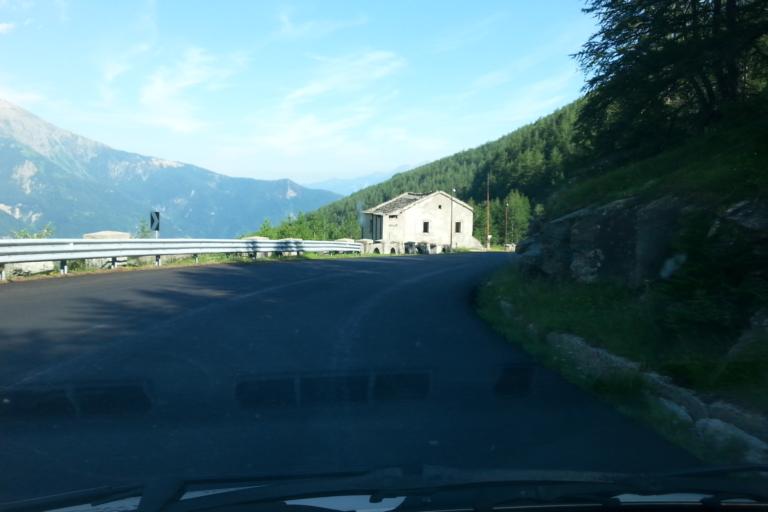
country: IT
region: Piedmont
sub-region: Provincia di Torino
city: Moncenisio
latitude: 45.2039
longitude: 6.9674
